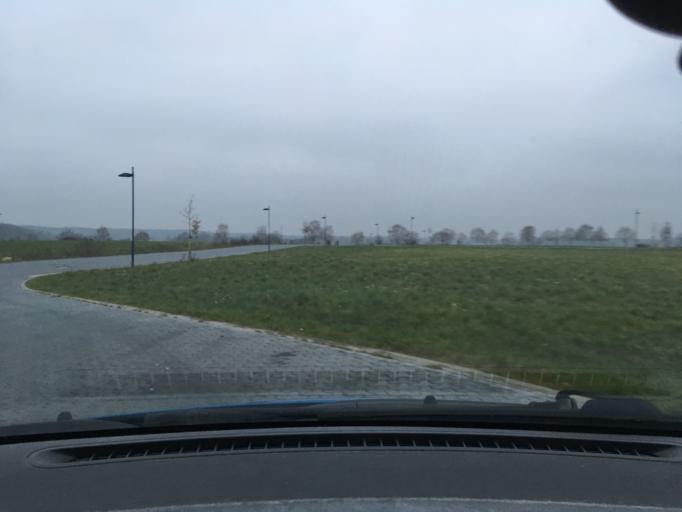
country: DE
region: Lower Saxony
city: Bispingen
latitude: 53.0976
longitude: 9.9874
